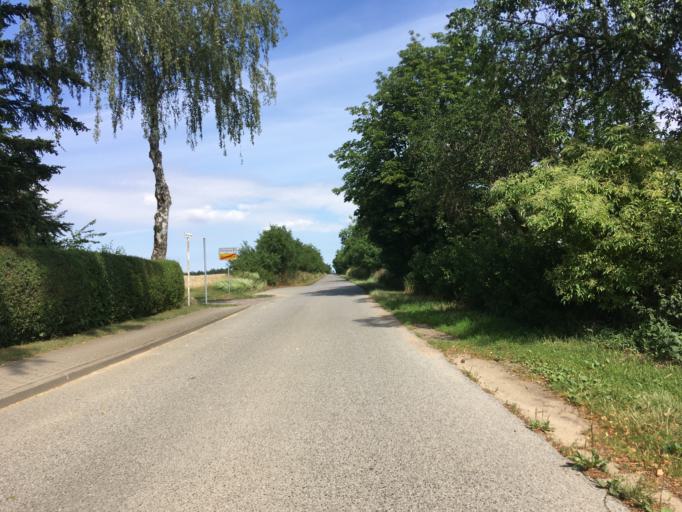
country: DE
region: Brandenburg
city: Casekow
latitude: 53.2101
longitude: 14.1500
